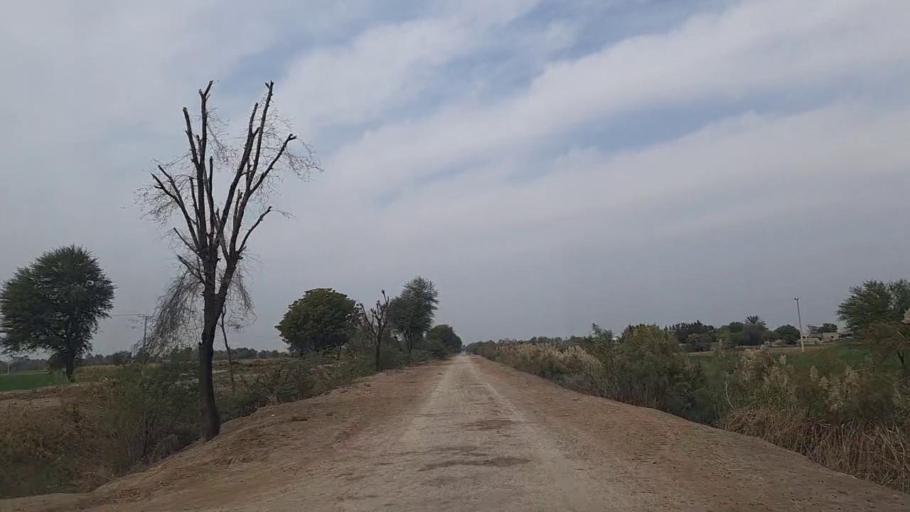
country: PK
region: Sindh
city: Daur
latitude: 26.4369
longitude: 68.4625
